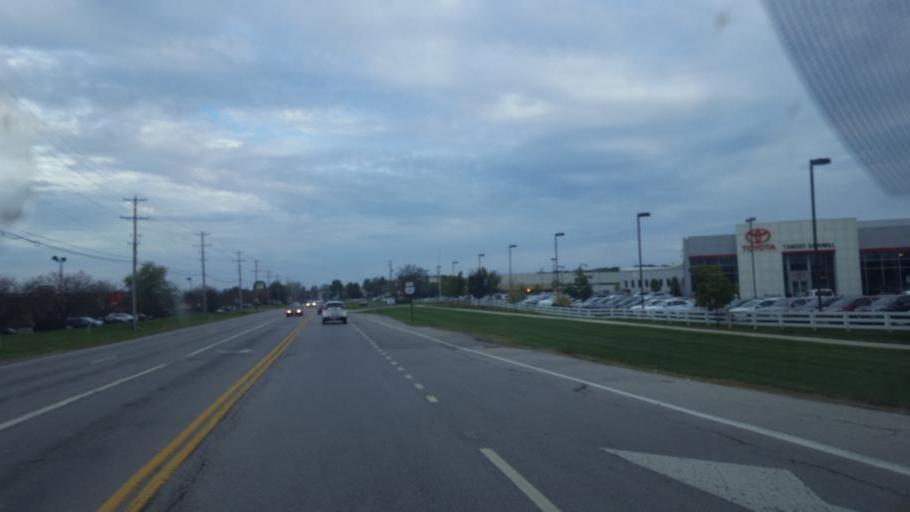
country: US
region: Ohio
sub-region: Franklin County
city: Dublin
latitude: 40.0967
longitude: -83.0910
